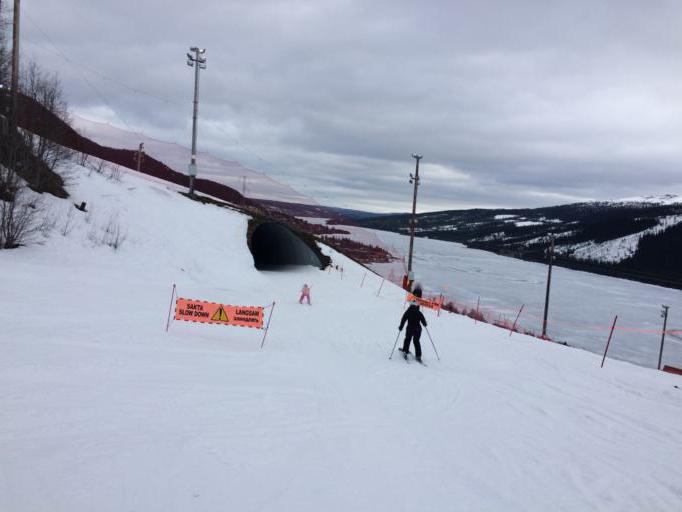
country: SE
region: Jaemtland
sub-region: Are Kommun
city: Are
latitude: 63.4071
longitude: 13.0565
